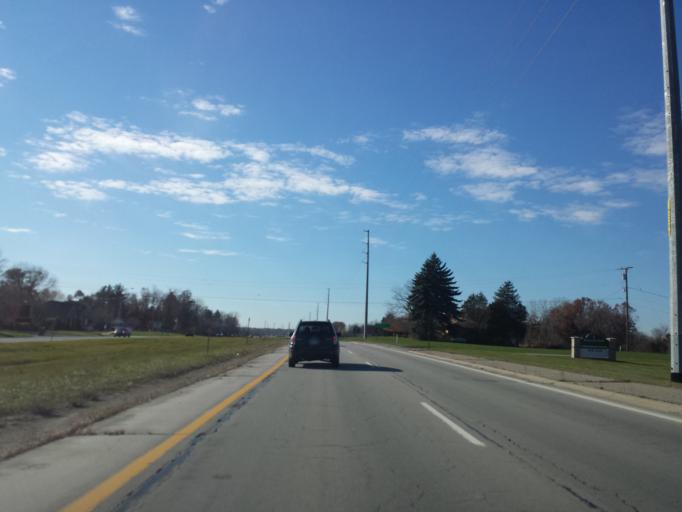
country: US
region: Michigan
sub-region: Livingston County
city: Brighton
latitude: 42.6363
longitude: -83.7274
